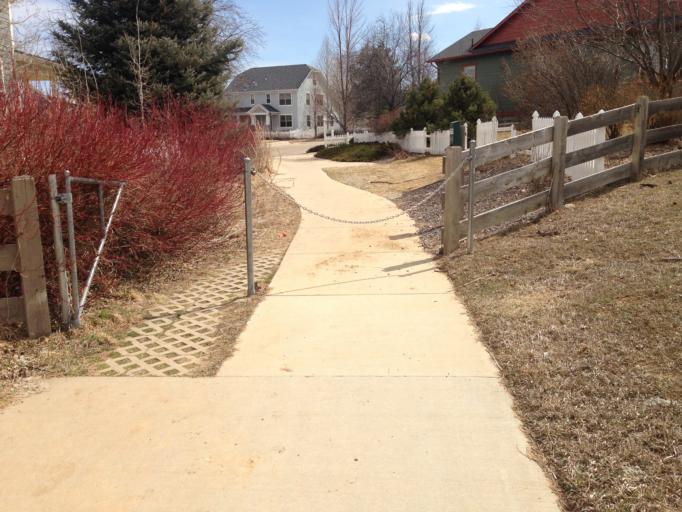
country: US
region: Colorado
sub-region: Boulder County
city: Louisville
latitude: 40.0072
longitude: -105.1406
